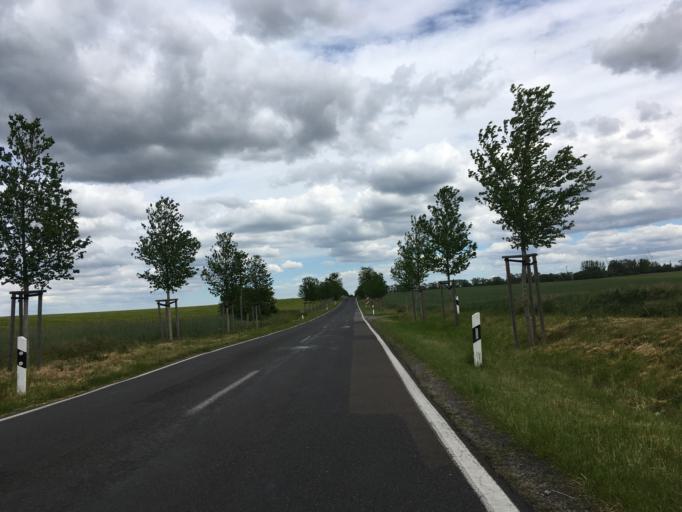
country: DE
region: Brandenburg
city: Hohenfinow
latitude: 52.7479
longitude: 13.8586
